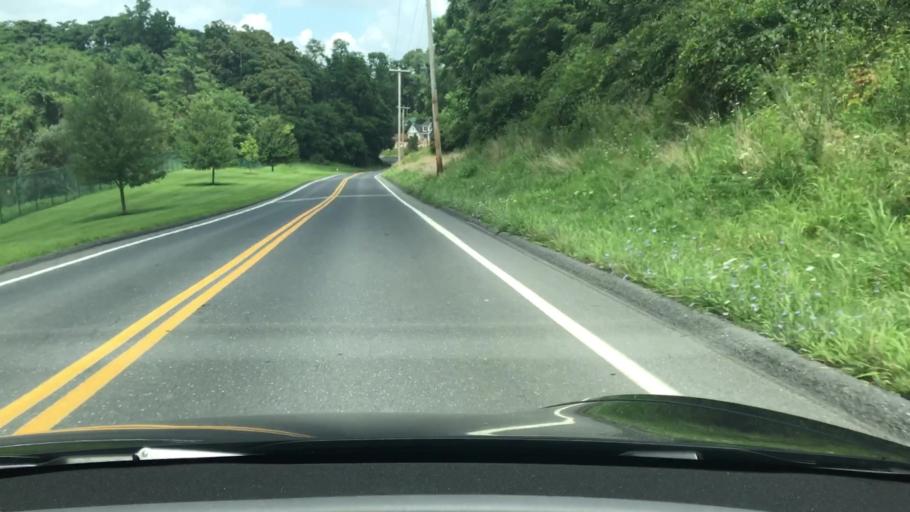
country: US
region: Pennsylvania
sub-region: Cumberland County
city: New Cumberland
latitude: 40.1987
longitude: -76.8783
